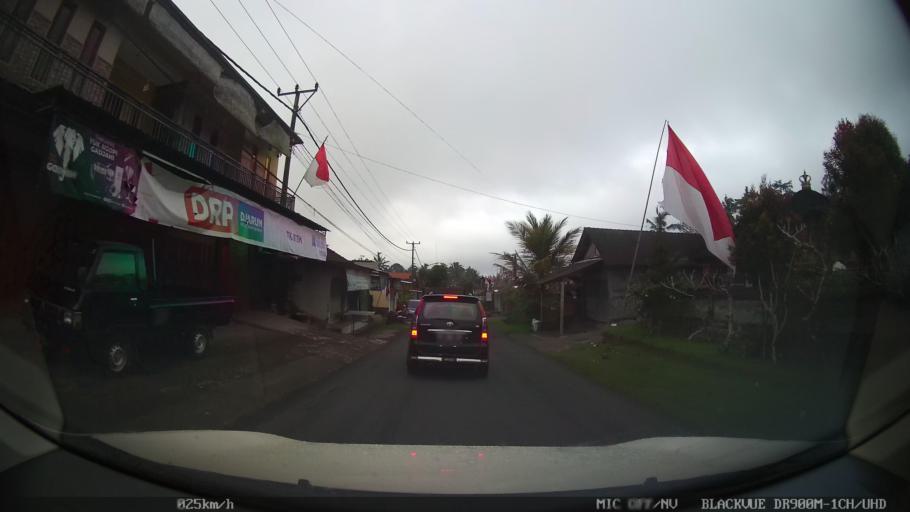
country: ID
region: Bali
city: Banjar Ponggang
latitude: -8.3889
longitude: 115.2612
